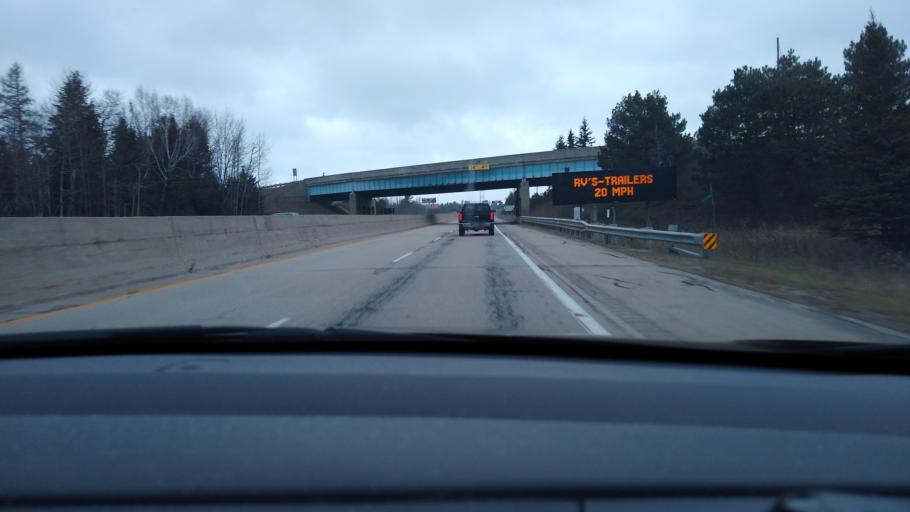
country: US
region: Michigan
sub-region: Mackinac County
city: Saint Ignace
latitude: 45.7714
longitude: -84.7346
